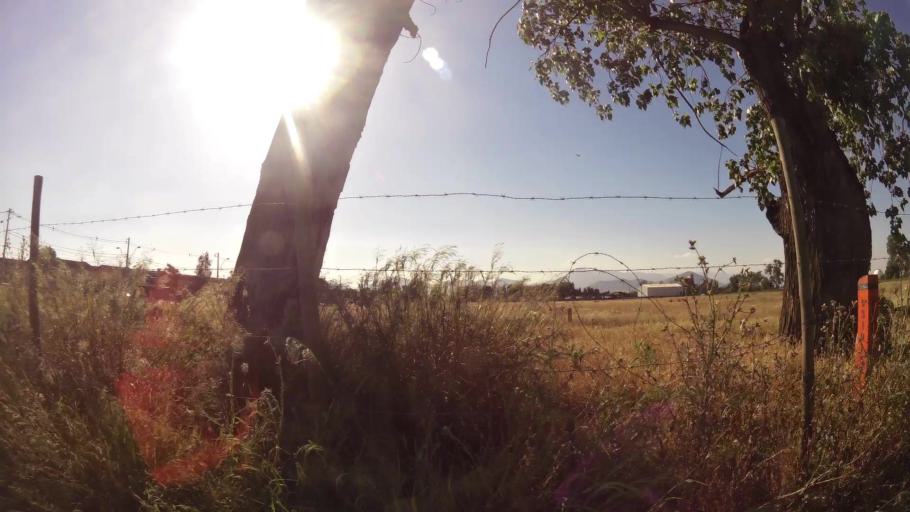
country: CL
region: Santiago Metropolitan
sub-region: Provincia de Maipo
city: San Bernardo
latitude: -33.5462
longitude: -70.7578
